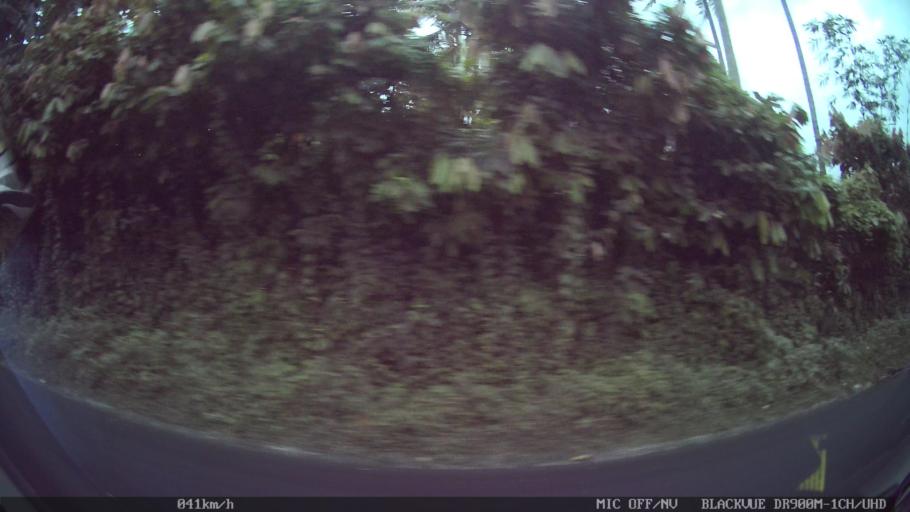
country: ID
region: Bali
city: Banjar Parekan
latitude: -8.5632
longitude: 115.2093
